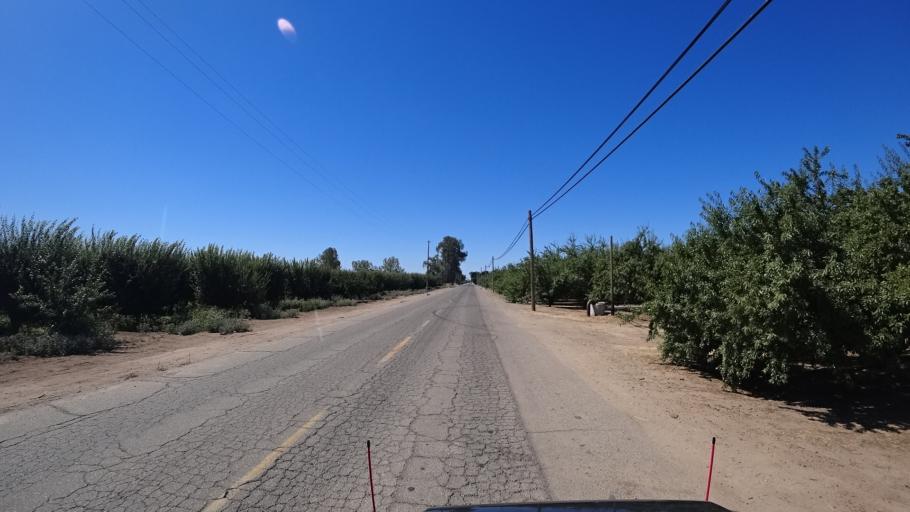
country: US
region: California
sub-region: Fresno County
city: West Park
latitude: 36.6972
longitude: -119.8089
